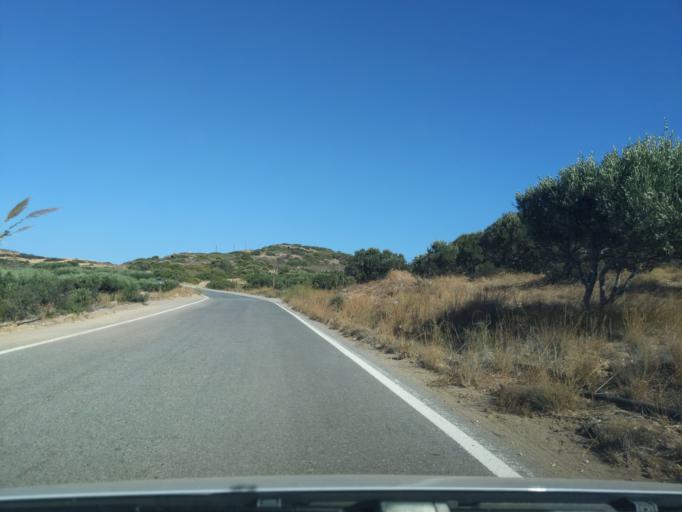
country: GR
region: Crete
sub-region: Nomos Lasithiou
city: Palekastro
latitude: 35.2234
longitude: 26.2588
